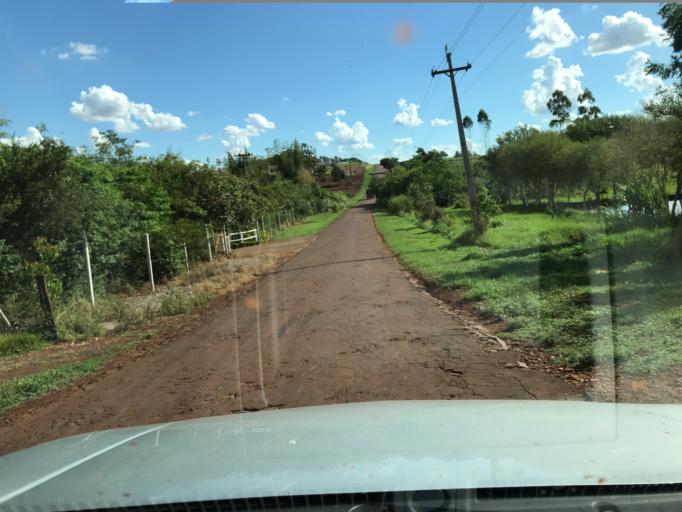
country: BR
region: Parana
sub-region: Palotina
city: Palotina
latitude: -24.2562
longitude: -53.7971
